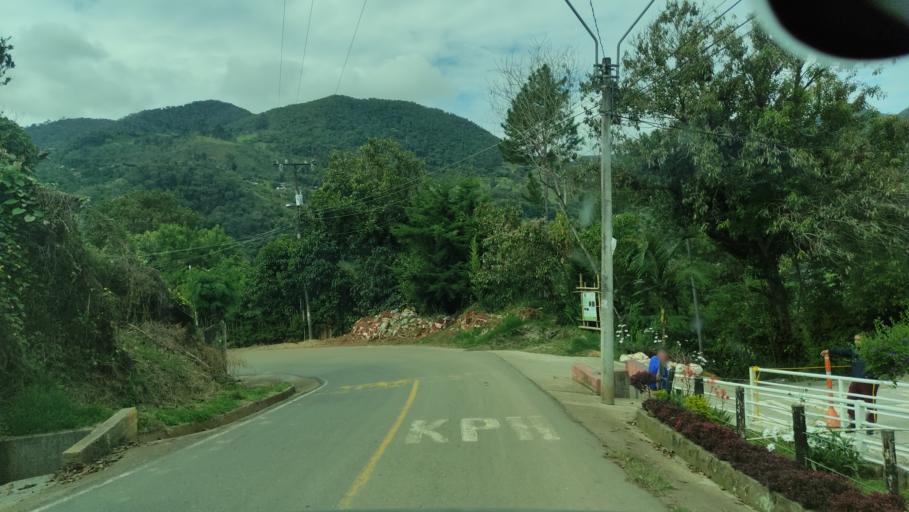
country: CO
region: Valle del Cauca
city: Cali
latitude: 3.4546
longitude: -76.6346
